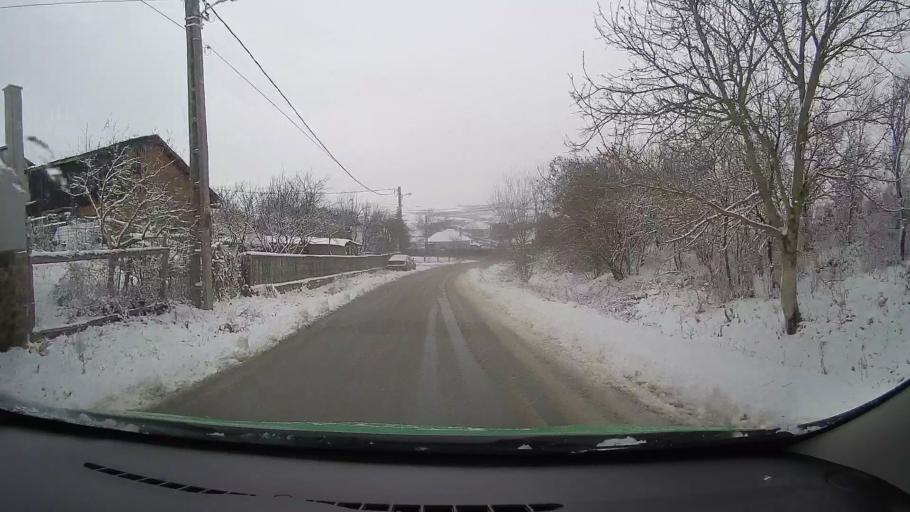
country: RO
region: Hunedoara
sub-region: Municipiul Hunedoara
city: Pestisu Mare
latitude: 45.8037
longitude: 22.9224
